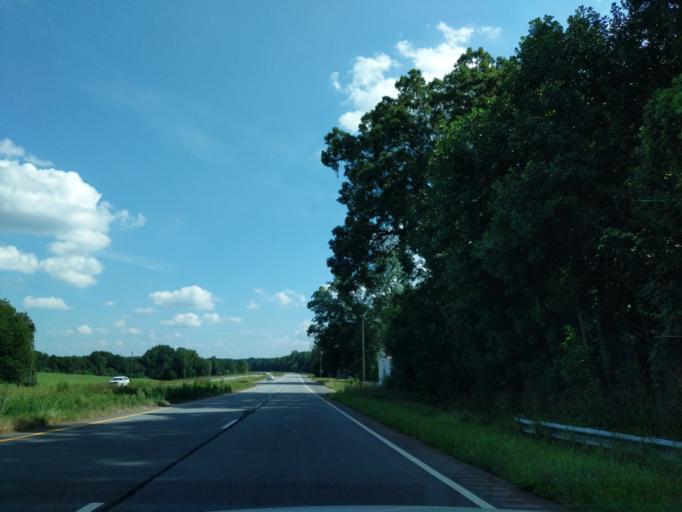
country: US
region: Georgia
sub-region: Habersham County
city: Baldwin
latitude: 34.4374
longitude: -83.5066
